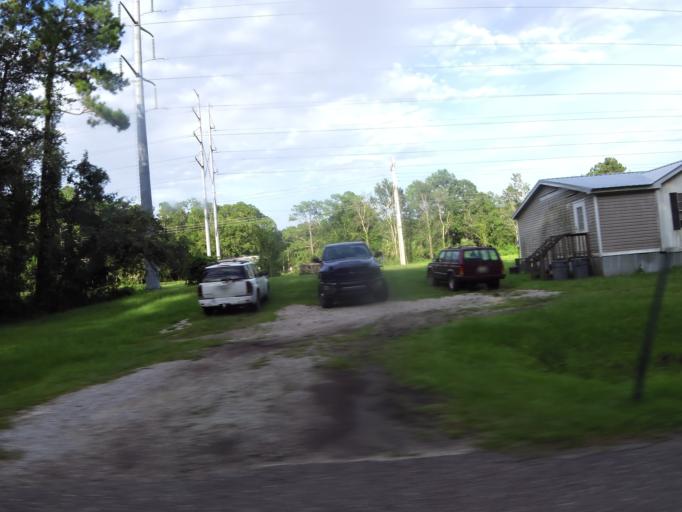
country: US
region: Florida
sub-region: Nassau County
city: Nassau Village-Ratliff
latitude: 30.3993
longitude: -81.7823
